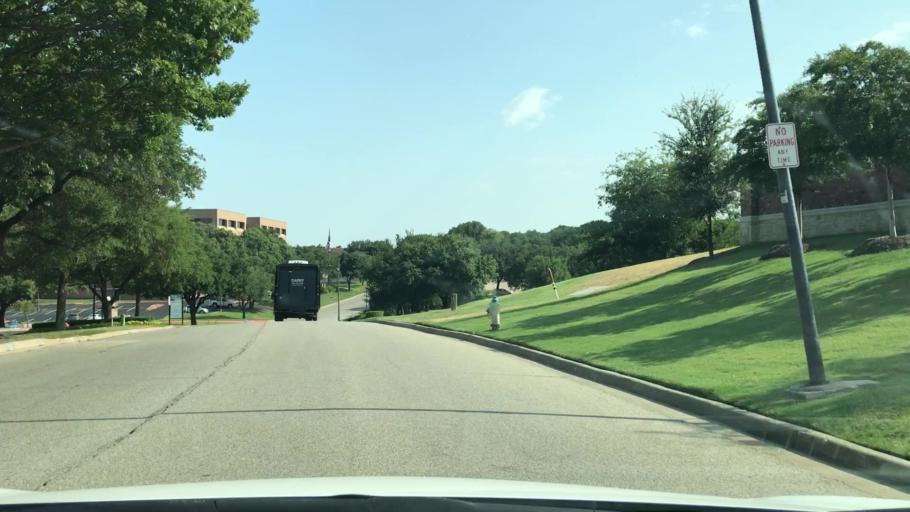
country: US
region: Texas
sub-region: Dallas County
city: Irving
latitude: 32.8703
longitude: -96.9482
